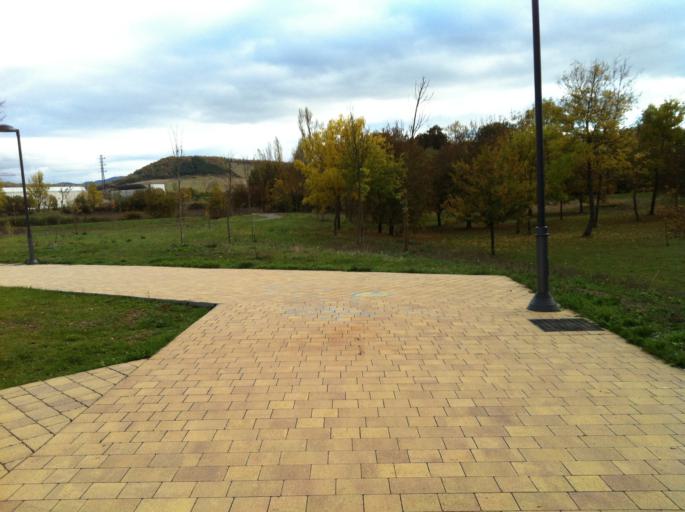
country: ES
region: Basque Country
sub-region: Provincia de Alava
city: Gasteiz / Vitoria
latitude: 42.8298
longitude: -2.6589
